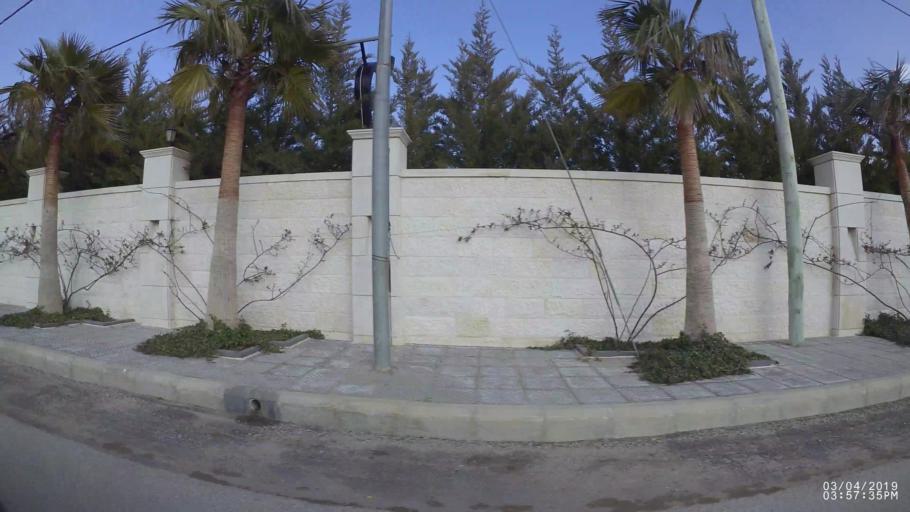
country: JO
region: Amman
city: Al Bunayyat ash Shamaliyah
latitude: 31.9107
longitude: 35.8726
